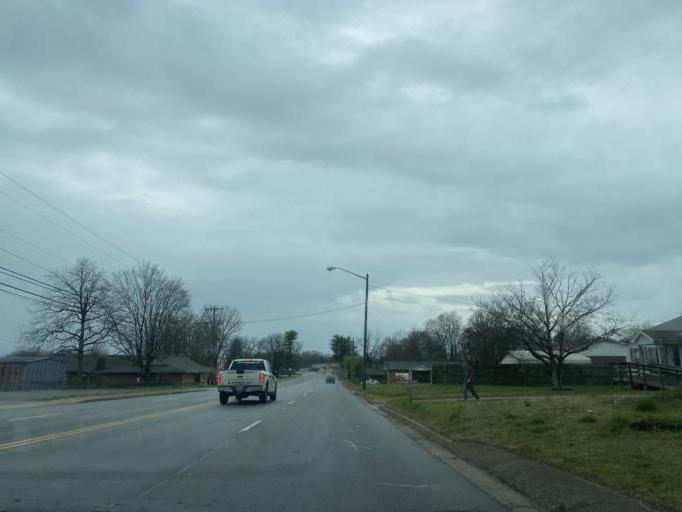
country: US
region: South Carolina
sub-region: Cherokee County
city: Gaffney
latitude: 35.0605
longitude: -81.6735
